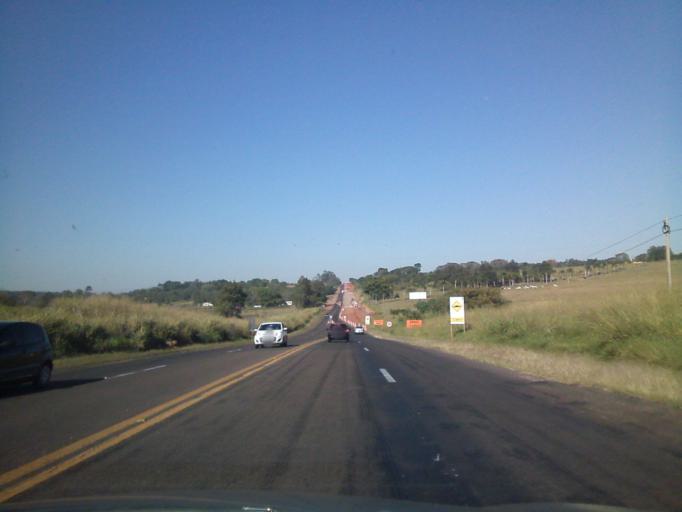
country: BR
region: Sao Paulo
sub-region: Pirapozinho
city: Pirapozinho
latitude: -22.2122
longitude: -51.4368
